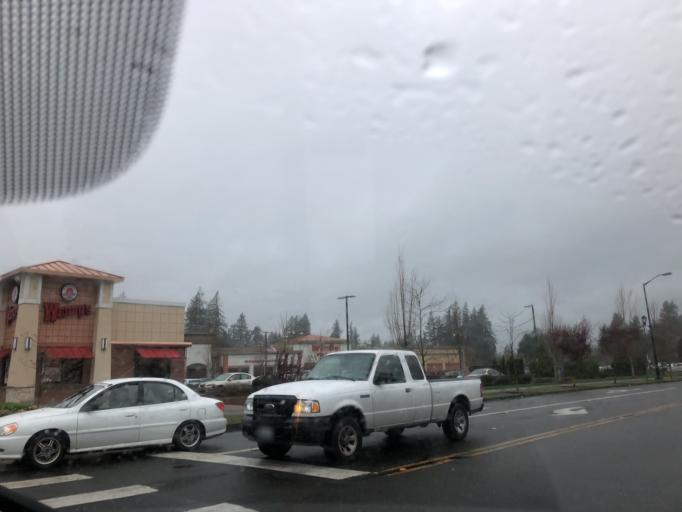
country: US
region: Washington
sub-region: Thurston County
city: Tanglewilde-Thompson Place
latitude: 47.0543
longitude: -122.7775
